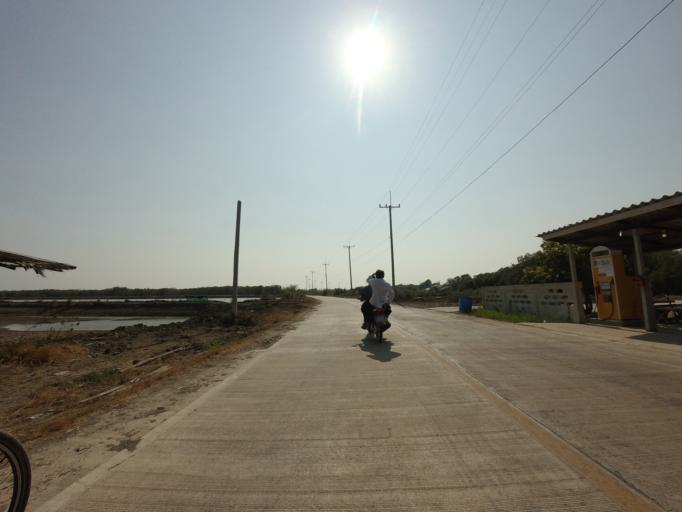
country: TH
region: Samut Sakhon
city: Samut Sakhon
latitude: 13.4982
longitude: 100.3336
